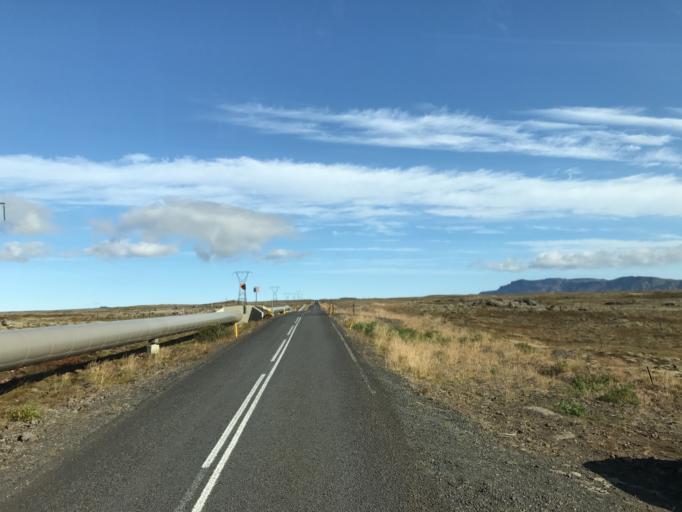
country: IS
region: Capital Region
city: Mosfellsbaer
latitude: 64.1087
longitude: -21.5762
